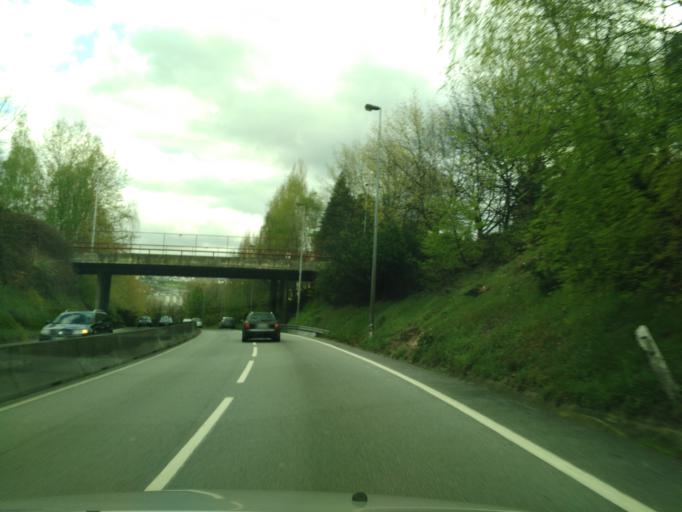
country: PT
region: Braga
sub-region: Guimaraes
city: Guimaraes
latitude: 41.4443
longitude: -8.3091
